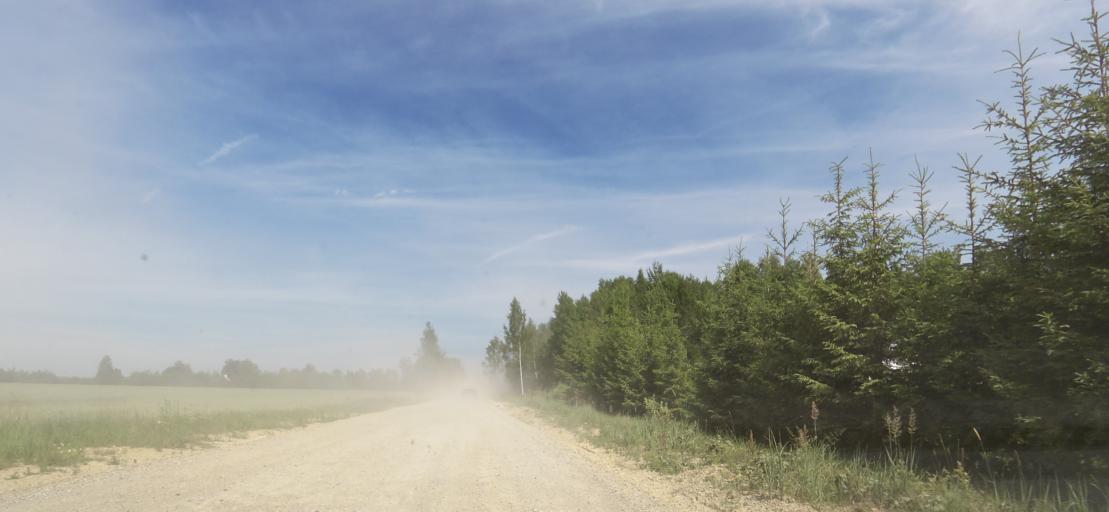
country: LT
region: Panevezys
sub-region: Panevezys City
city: Panevezys
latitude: 55.7206
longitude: 24.2895
